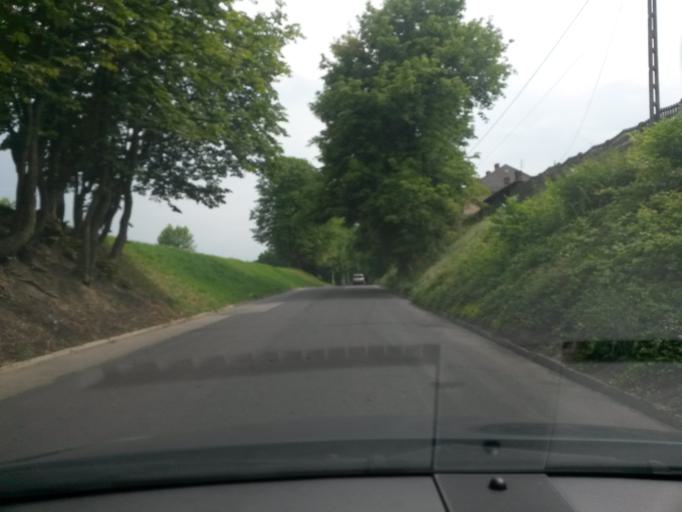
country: PL
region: Silesian Voivodeship
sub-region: Powiat czestochowski
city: Huta Stara B
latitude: 50.7642
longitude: 19.1541
